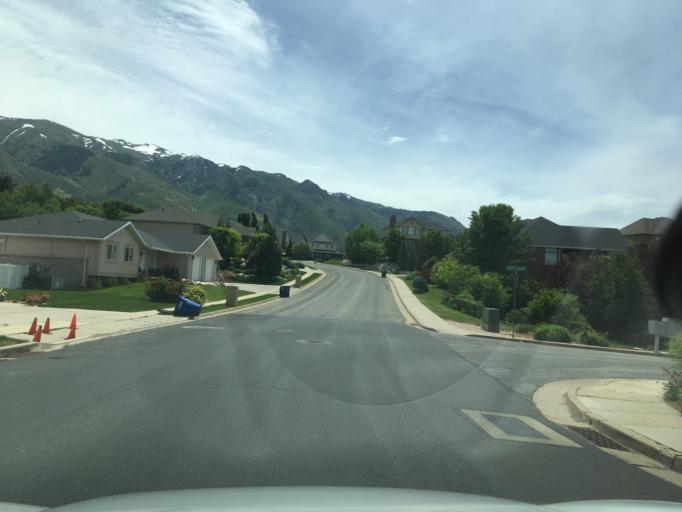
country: US
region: Utah
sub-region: Davis County
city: South Weber
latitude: 41.1023
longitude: -111.9262
